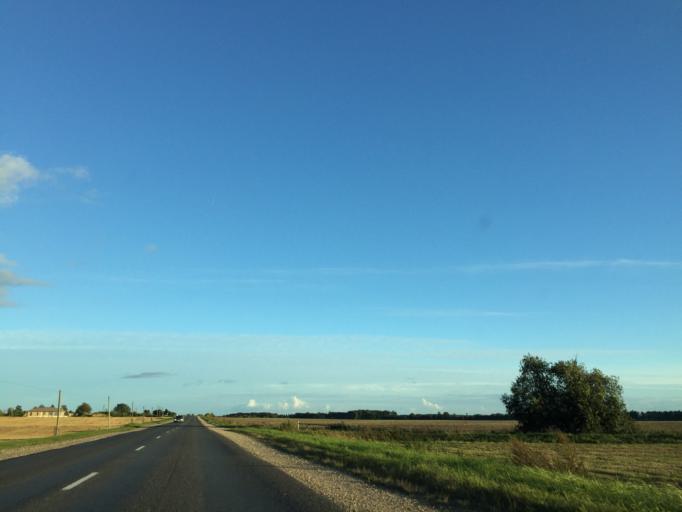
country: LV
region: Saldus Rajons
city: Saldus
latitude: 56.7012
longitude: 22.4304
